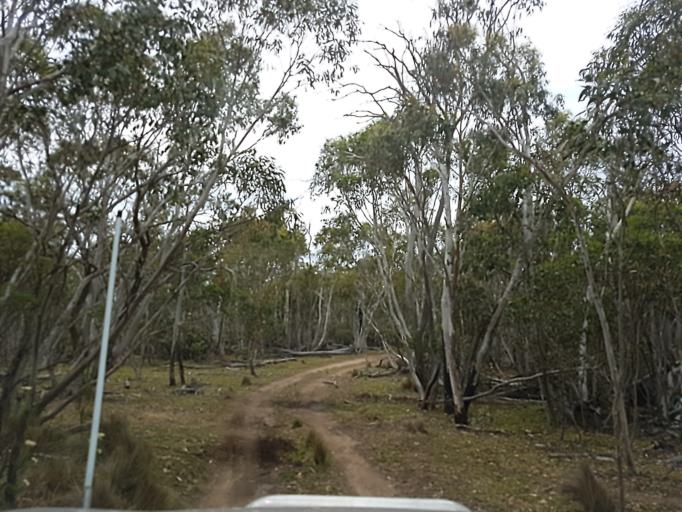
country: AU
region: New South Wales
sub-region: Snowy River
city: Jindabyne
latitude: -36.8585
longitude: 148.2646
